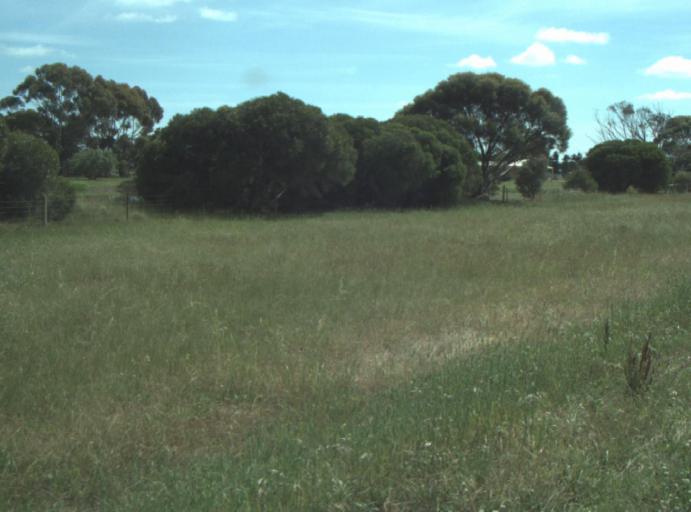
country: AU
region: Victoria
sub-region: Greater Geelong
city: Lara
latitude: -38.0186
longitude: 144.4456
